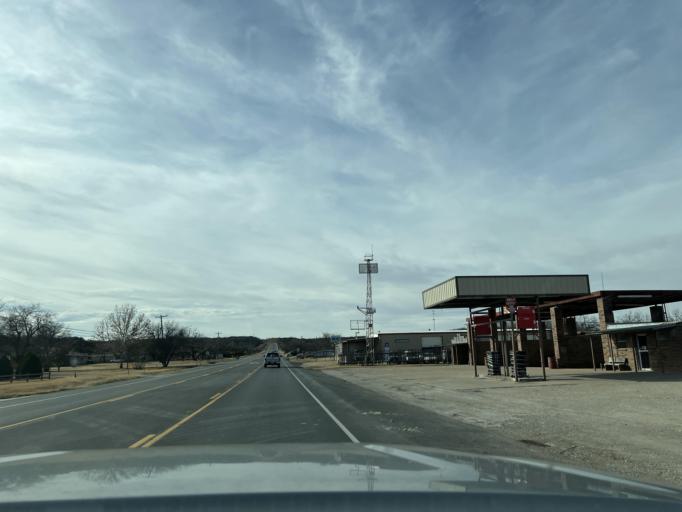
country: US
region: Texas
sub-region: Shackelford County
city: Albany
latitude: 32.7180
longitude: -99.3025
